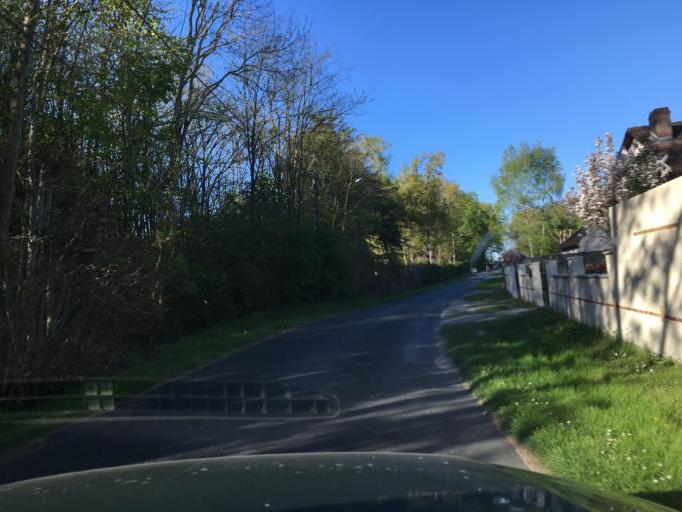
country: FR
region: Centre
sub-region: Departement du Loiret
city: Lailly-en-Val
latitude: 47.7638
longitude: 1.6809
